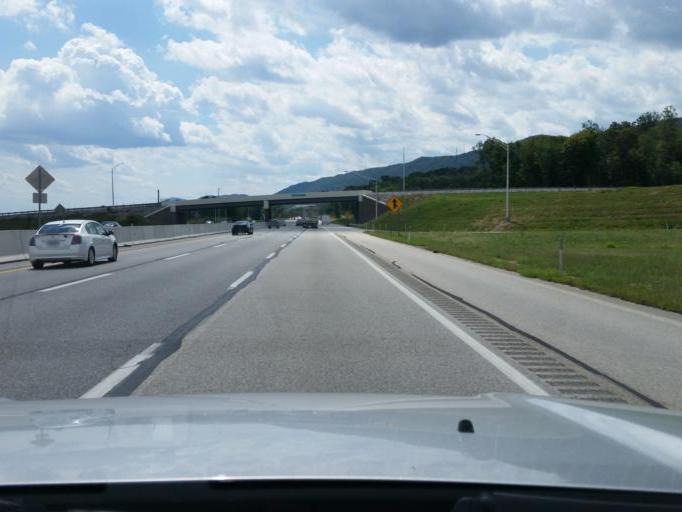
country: US
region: Pennsylvania
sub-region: Franklin County
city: Doylestown
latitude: 40.1597
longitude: -77.6125
